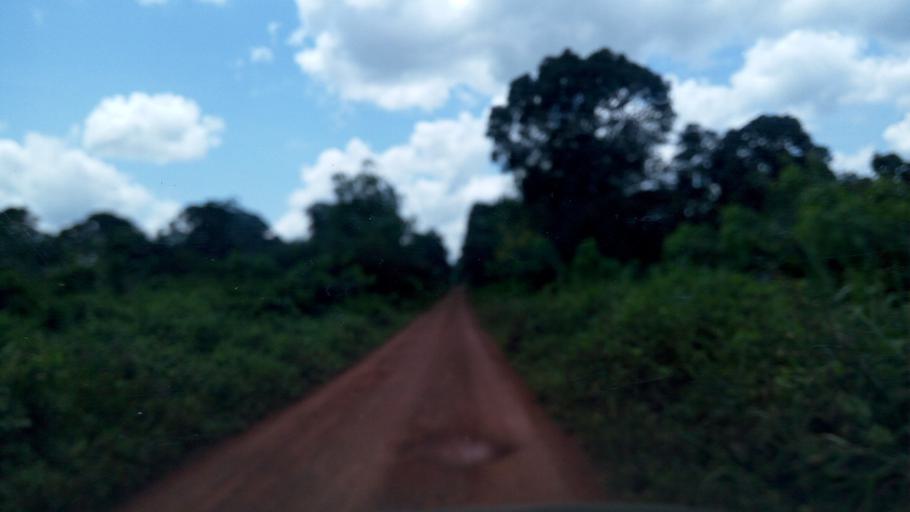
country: CD
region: Equateur
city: Libenge
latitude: 3.7269
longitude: 18.7633
